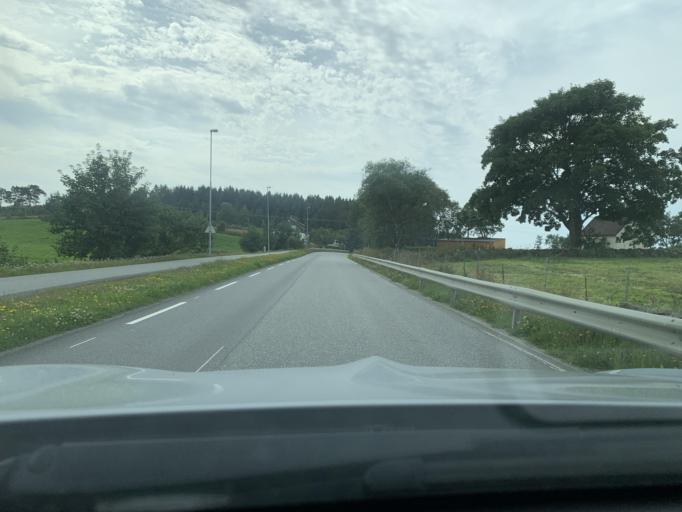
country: NO
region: Rogaland
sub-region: Time
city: Bryne
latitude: 58.7388
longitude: 5.6868
